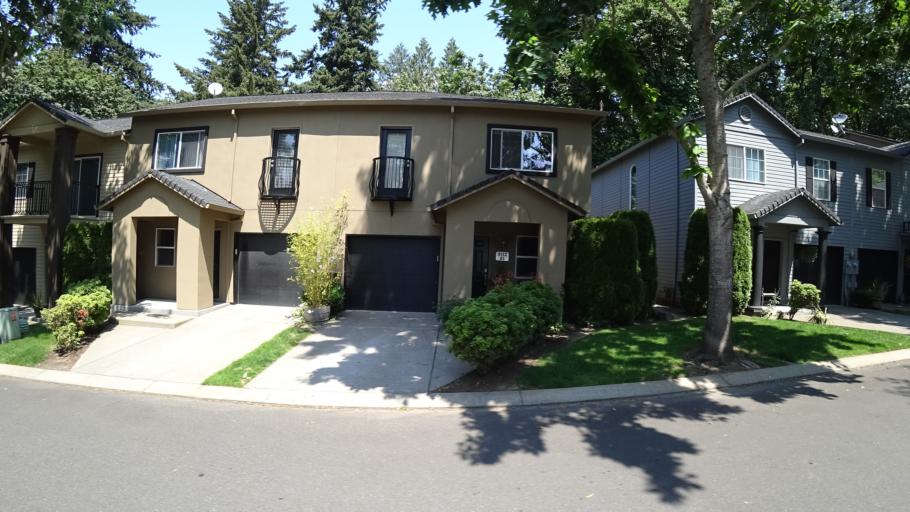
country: US
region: Oregon
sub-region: Multnomah County
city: Lents
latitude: 45.4646
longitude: -122.5616
